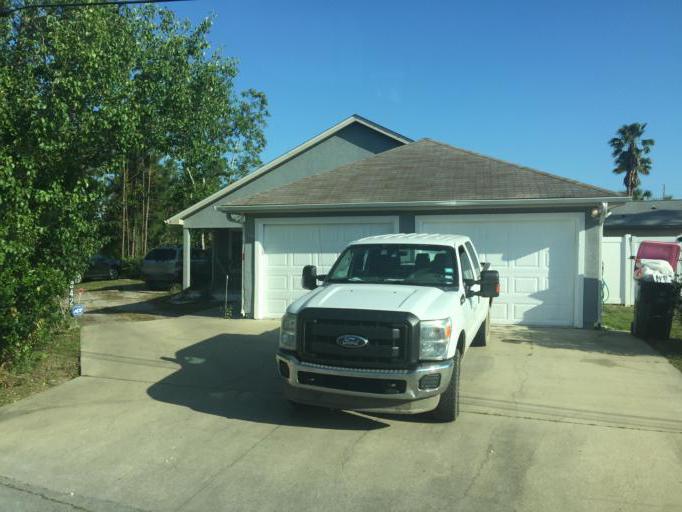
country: US
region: Florida
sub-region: Bay County
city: Panama City Beach
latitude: 30.2061
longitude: -85.8273
